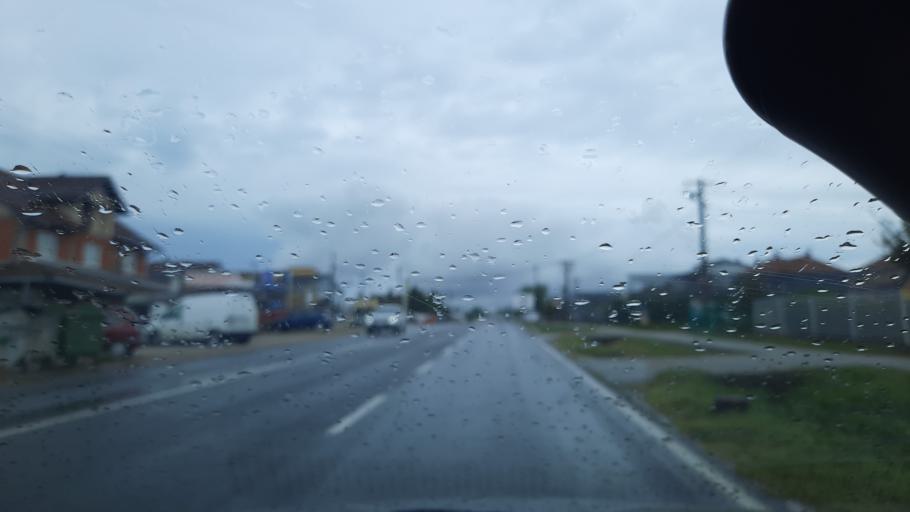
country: RS
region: Central Serbia
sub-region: Sumadijski Okrug
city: Kragujevac
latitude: 43.9891
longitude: 20.8513
